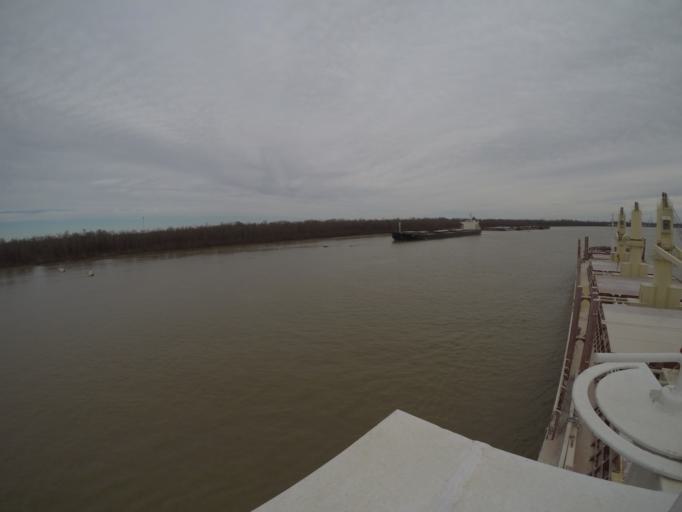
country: US
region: Louisiana
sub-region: Saint John the Baptist Parish
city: Montegut
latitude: 30.0522
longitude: -90.4982
